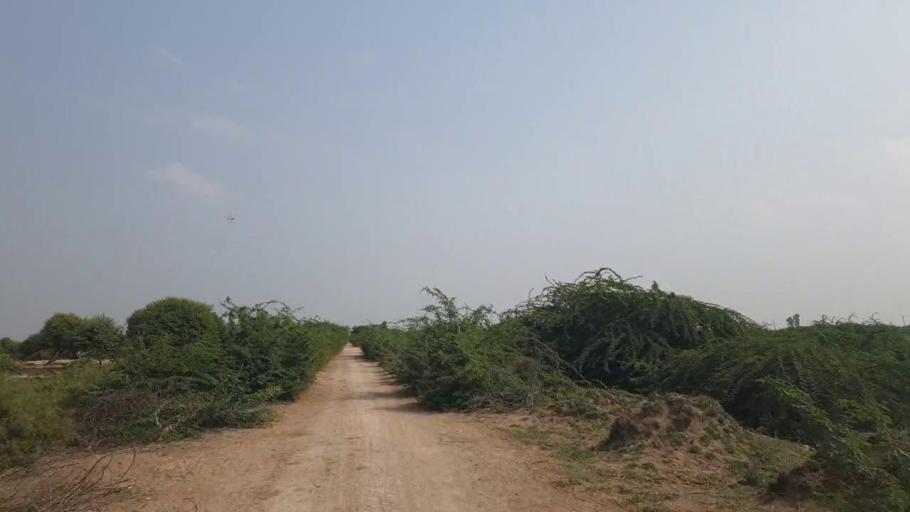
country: PK
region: Sindh
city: Badin
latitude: 24.5475
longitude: 68.7065
